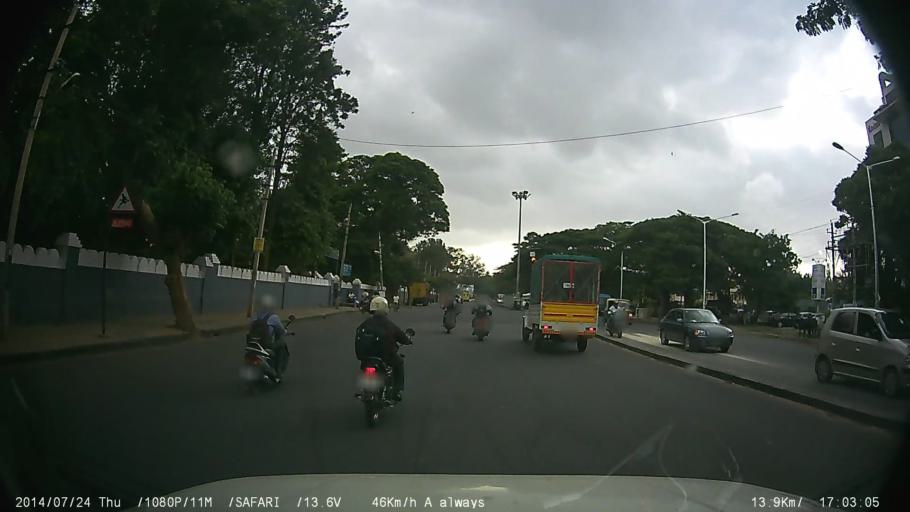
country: IN
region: Karnataka
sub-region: Bangalore Urban
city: Bangalore
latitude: 12.9245
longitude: 77.6320
